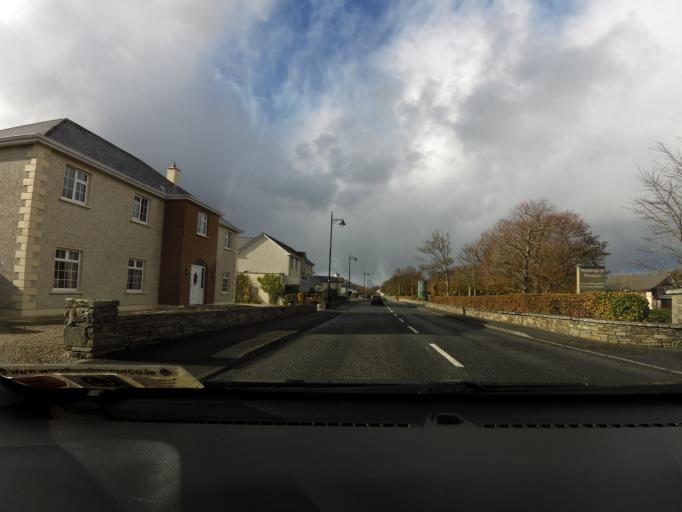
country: IE
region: Connaught
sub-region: Maigh Eo
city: Westport
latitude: 53.7988
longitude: -9.5394
